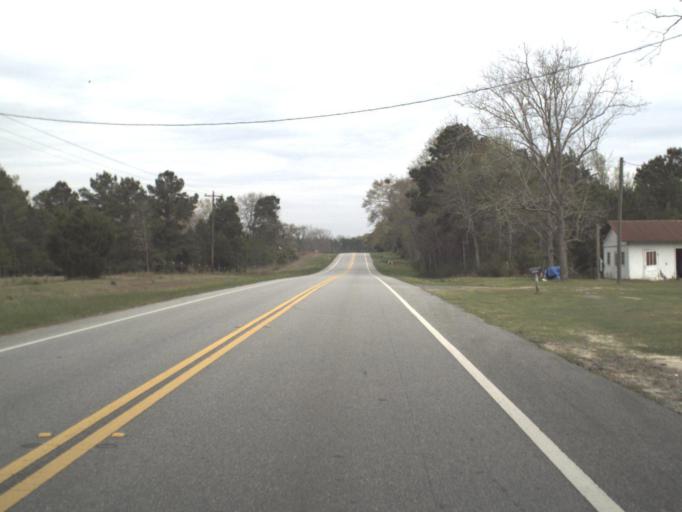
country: US
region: Florida
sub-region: Jackson County
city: Graceville
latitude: 30.9447
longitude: -85.6490
